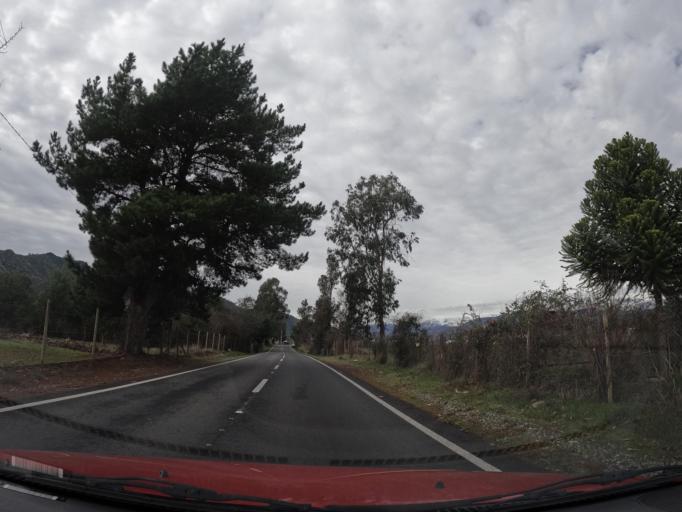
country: CL
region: Maule
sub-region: Provincia de Linares
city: Linares
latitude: -35.9257
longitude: -71.4194
